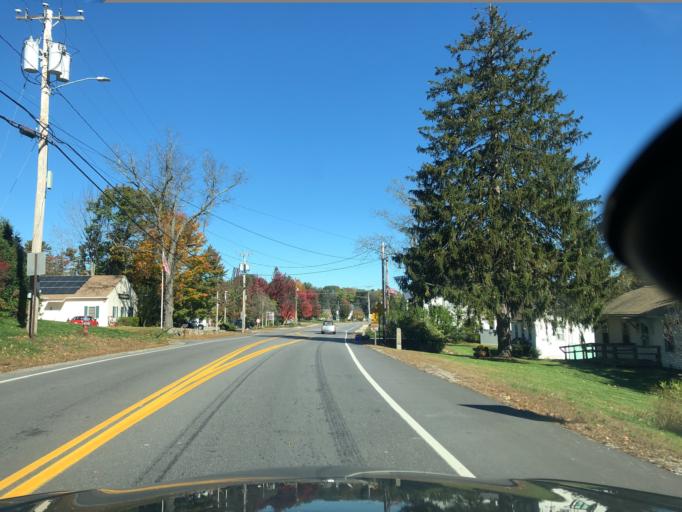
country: US
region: New Hampshire
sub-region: Rockingham County
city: Newmarket
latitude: 43.0691
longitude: -70.9395
